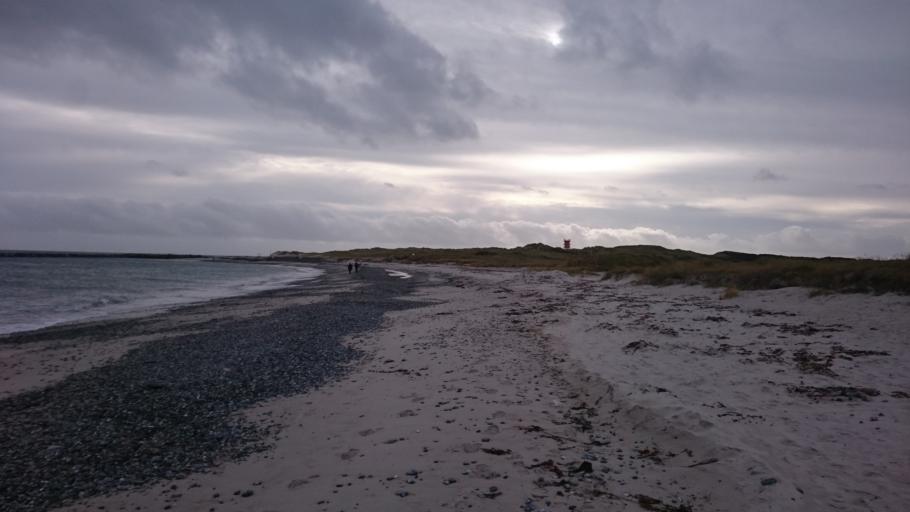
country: DE
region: Schleswig-Holstein
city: Helgoland
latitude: 54.1858
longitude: 7.9176
